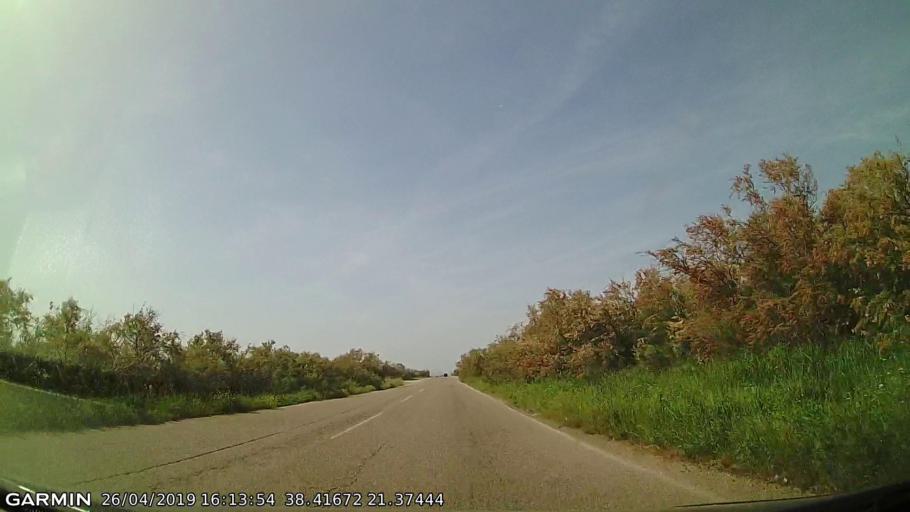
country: GR
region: West Greece
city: Aitoliko
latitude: 38.4170
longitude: 21.3742
